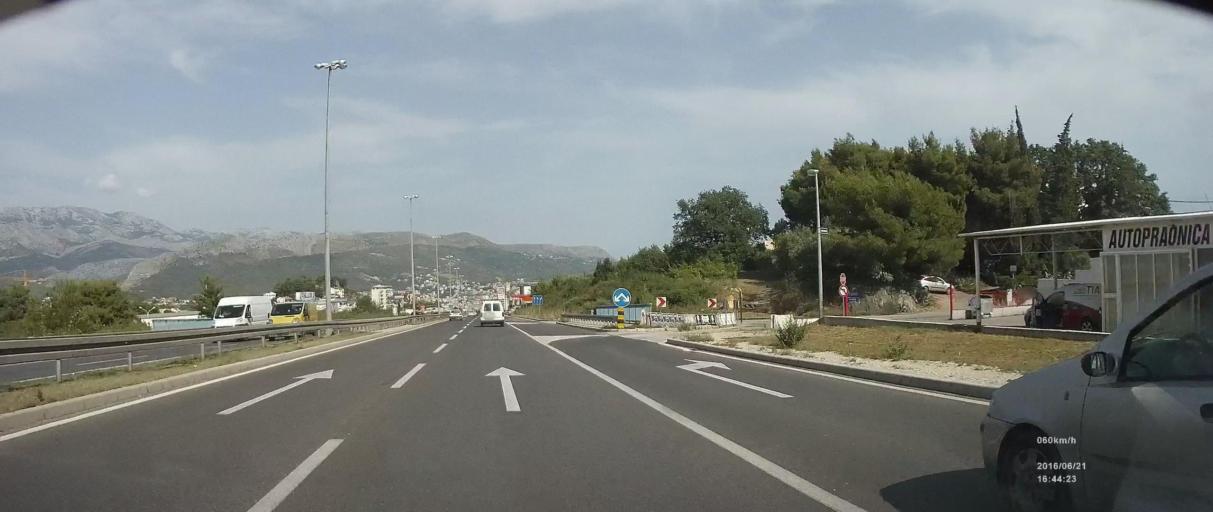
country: HR
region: Splitsko-Dalmatinska
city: Kamen
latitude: 43.5087
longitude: 16.4961
